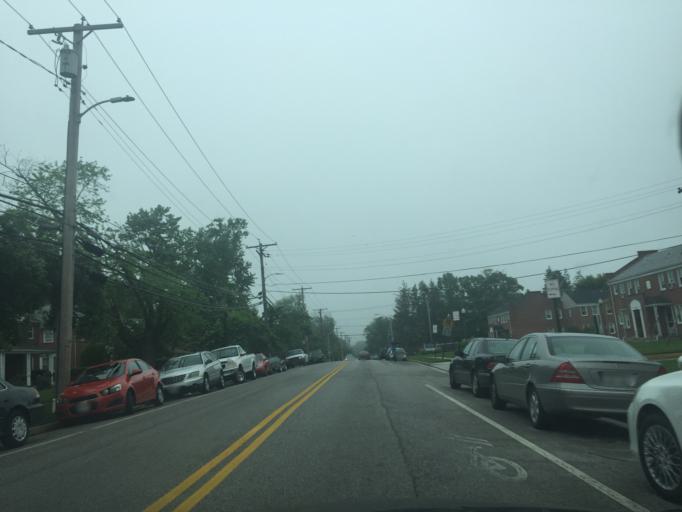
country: US
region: Maryland
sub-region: Baltimore County
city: Pikesville
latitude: 39.3588
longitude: -76.7043
